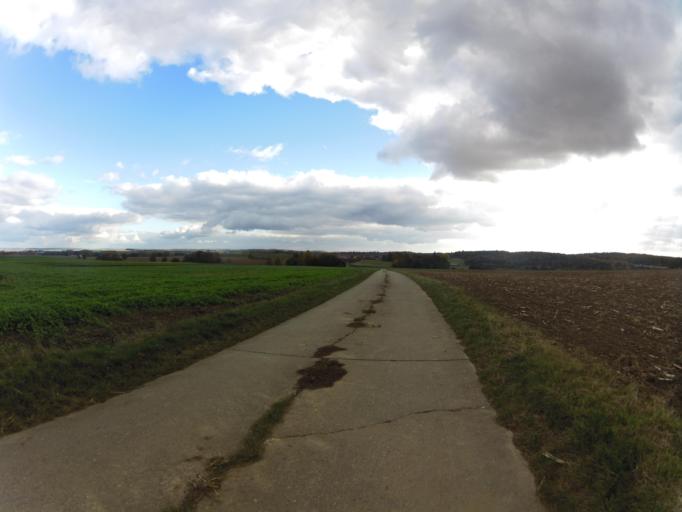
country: DE
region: Bavaria
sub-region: Regierungsbezirk Unterfranken
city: Kurnach
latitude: 49.8682
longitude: 10.0026
